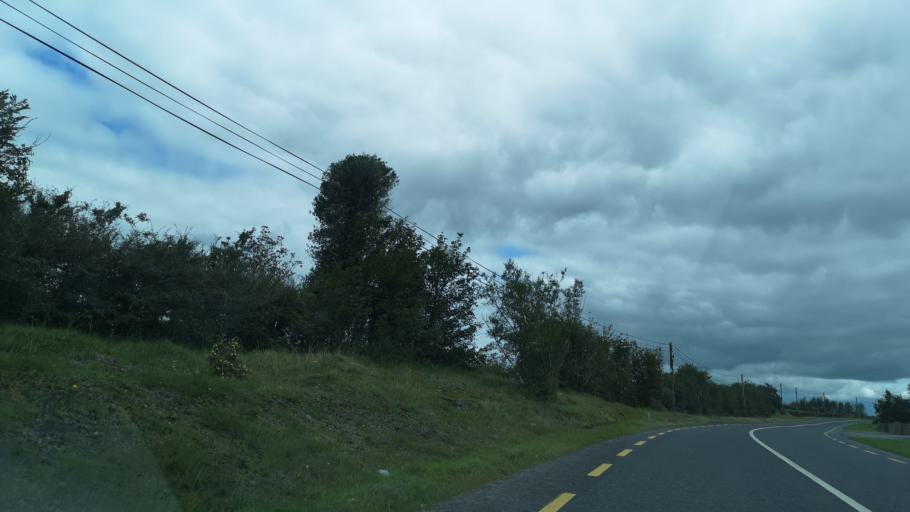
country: IE
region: Connaught
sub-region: County Galway
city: Ballinasloe
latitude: 53.3063
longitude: -8.1444
